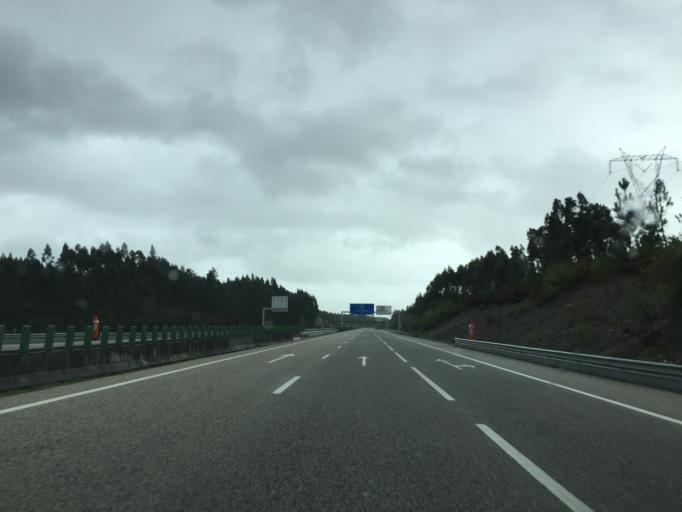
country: PT
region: Leiria
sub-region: Pombal
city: Lourical
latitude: 39.9502
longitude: -8.7712
